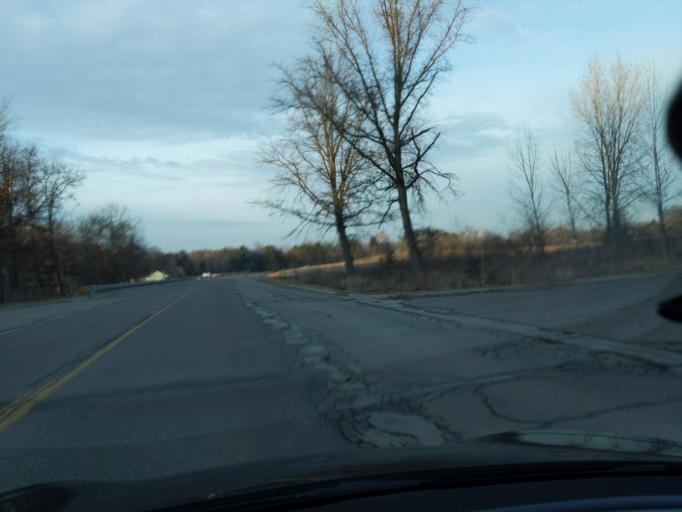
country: US
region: Michigan
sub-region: Livingston County
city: Brighton
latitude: 42.5928
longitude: -83.7539
